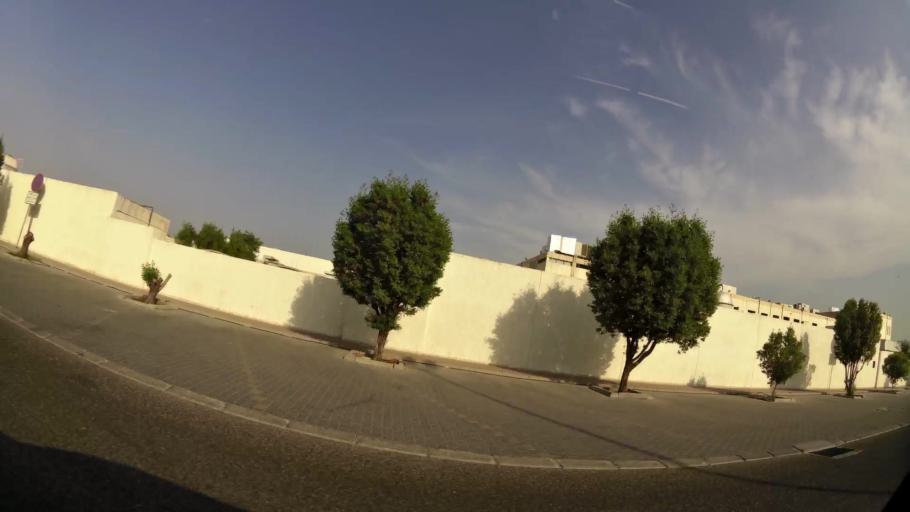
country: KW
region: Al Asimah
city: Ash Shamiyah
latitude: 29.3311
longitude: 47.9806
